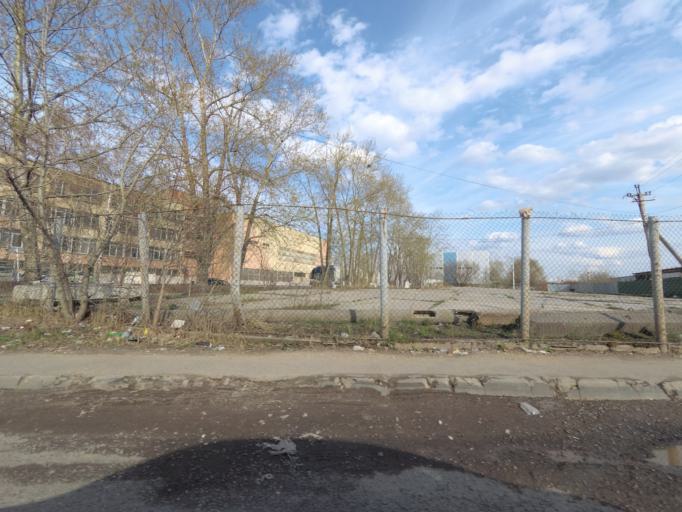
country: RU
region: Moskovskaya
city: Lobnya
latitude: 56.0188
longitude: 37.4360
